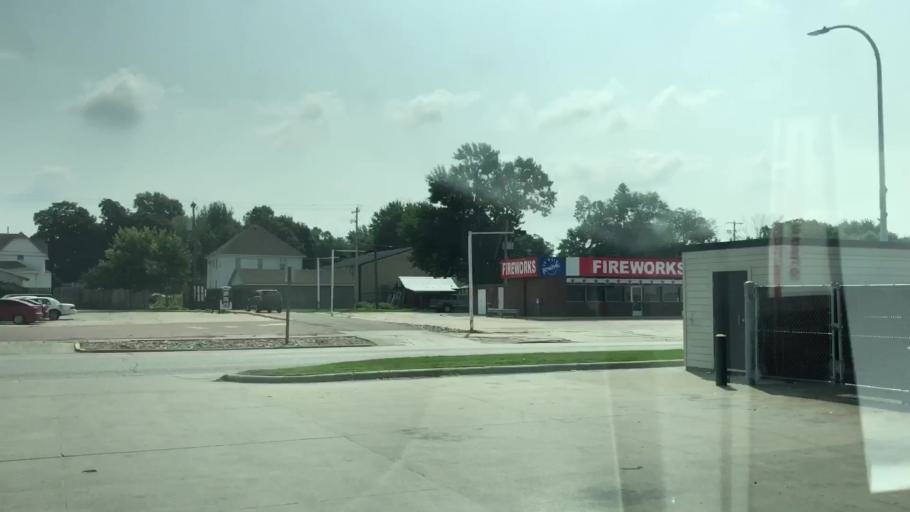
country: US
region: Iowa
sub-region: O'Brien County
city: Sheldon
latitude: 43.1855
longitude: -95.8547
